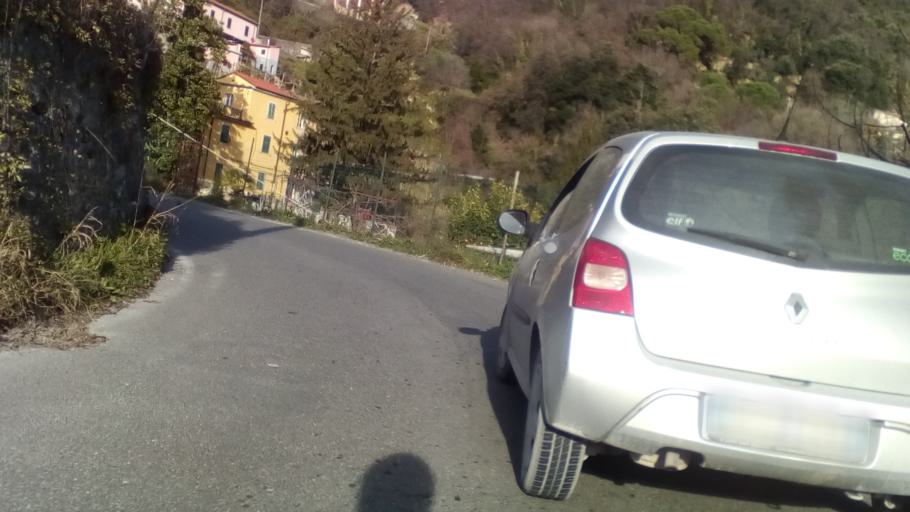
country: IT
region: Tuscany
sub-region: Provincia di Massa-Carrara
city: Massa
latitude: 44.0831
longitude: 10.1160
